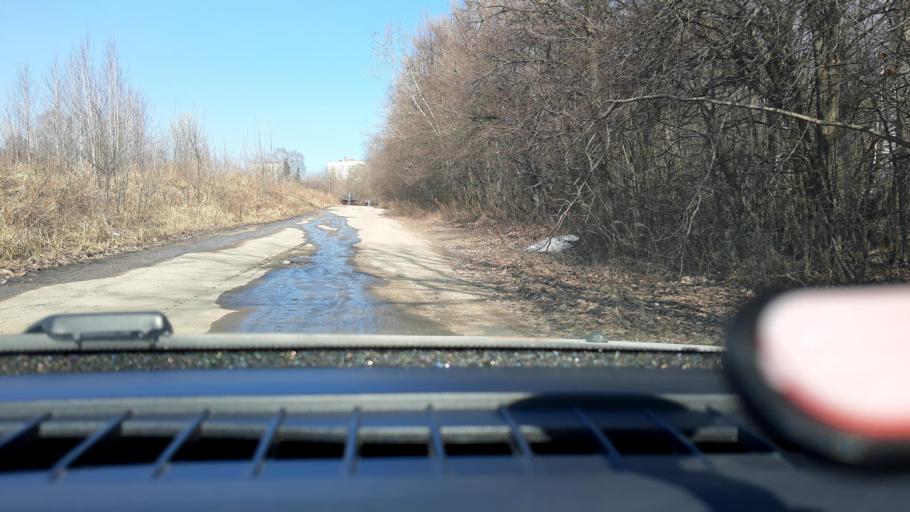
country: RU
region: Nizjnij Novgorod
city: Nizhniy Novgorod
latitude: 56.2539
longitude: 44.0031
